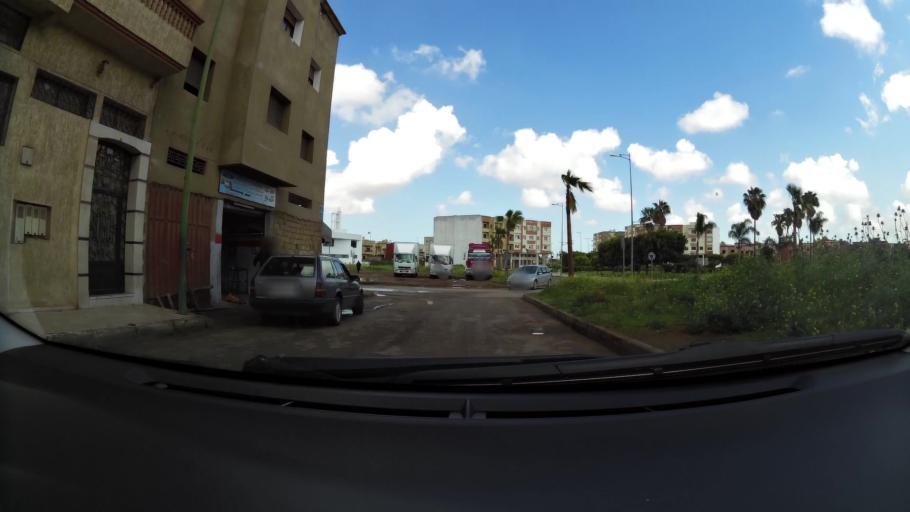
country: MA
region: Grand Casablanca
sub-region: Mediouna
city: Tit Mellil
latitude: 33.5528
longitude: -7.4848
